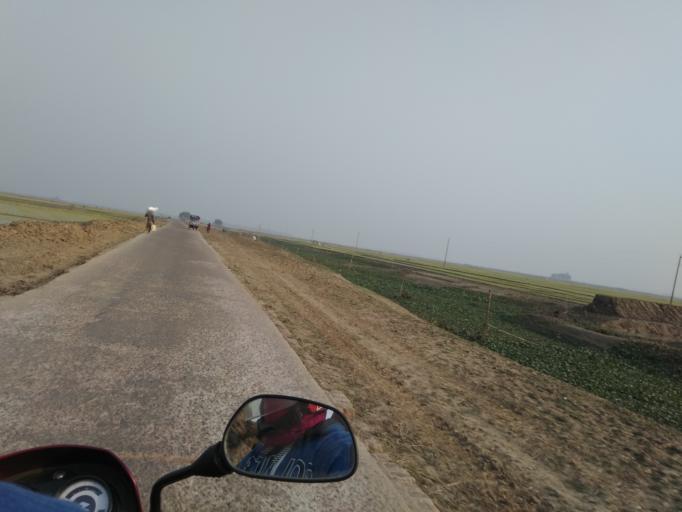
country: BD
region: Rajshahi
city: Ishurdi
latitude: 24.4890
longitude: 89.2043
